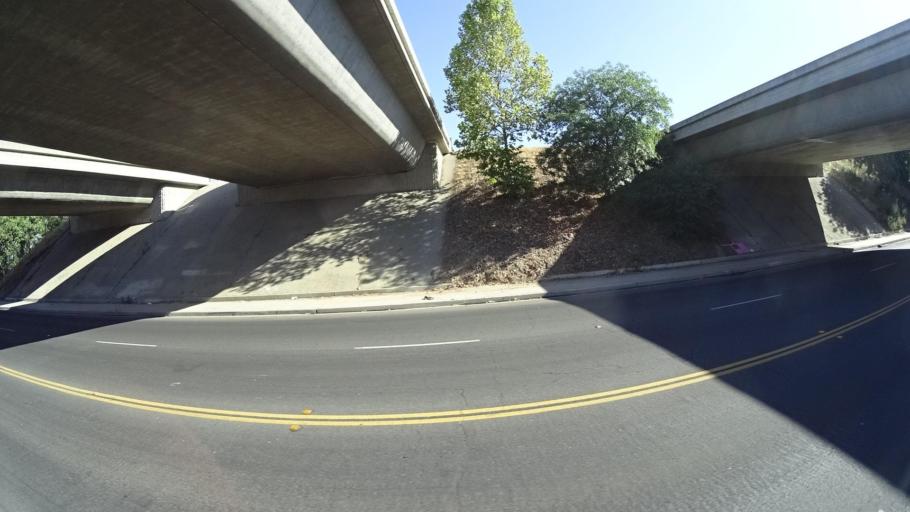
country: US
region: California
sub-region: Fresno County
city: Fresno
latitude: 36.7577
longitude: -119.7761
